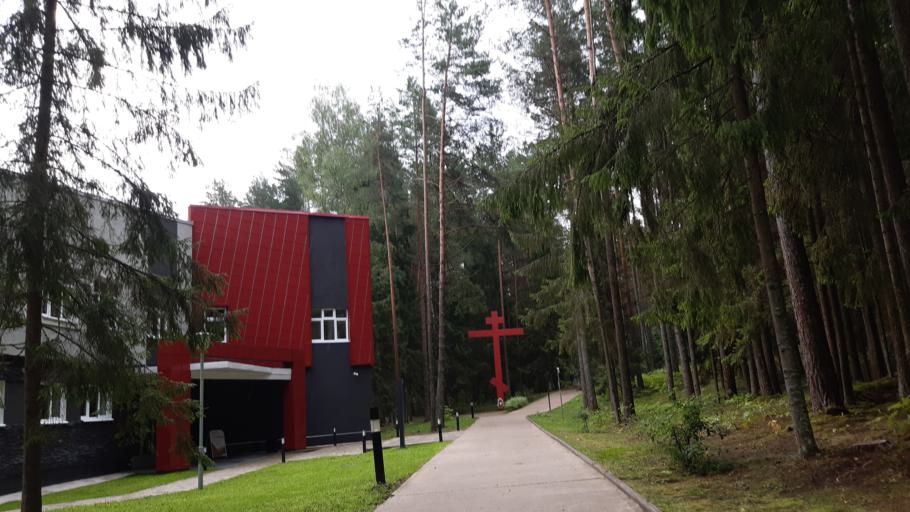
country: RU
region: Smolensk
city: Katyn'
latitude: 54.7746
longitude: 31.7896
